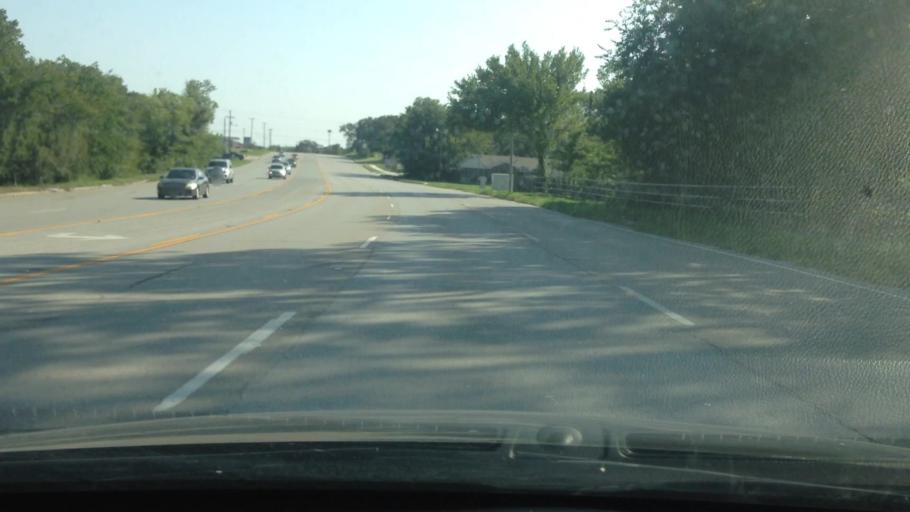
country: US
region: Texas
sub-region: Tarrant County
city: North Richland Hills
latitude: 32.8748
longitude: -97.2064
